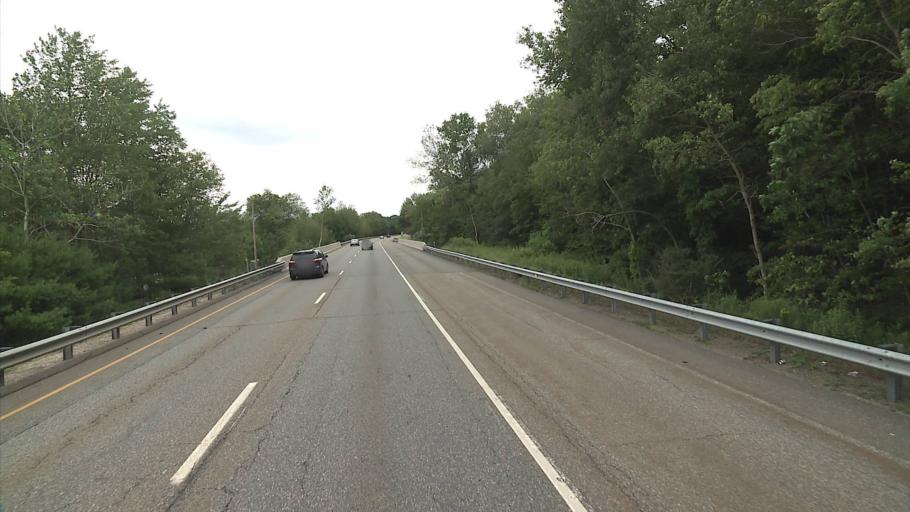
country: US
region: Connecticut
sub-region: Litchfield County
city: Northwest Harwinton
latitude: 41.7265
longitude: -73.1018
